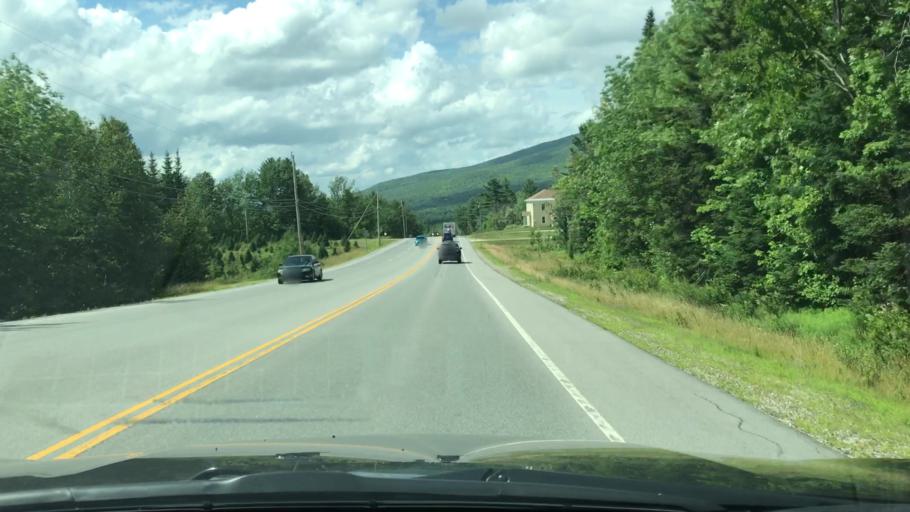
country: US
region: New Hampshire
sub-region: Coos County
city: Jefferson
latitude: 44.3750
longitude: -71.4109
